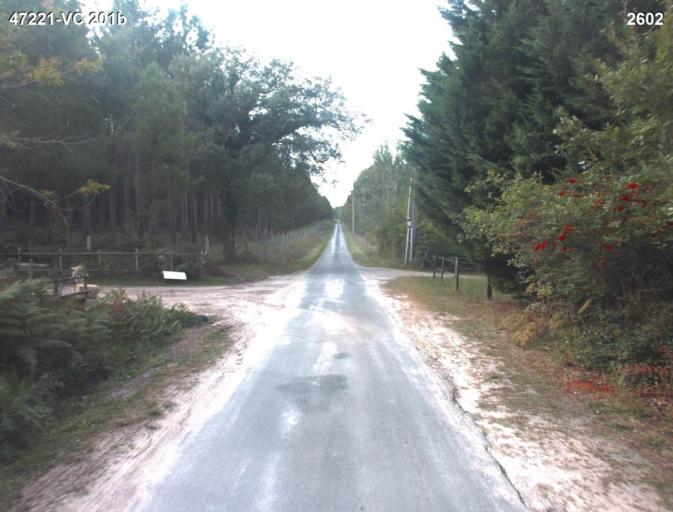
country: FR
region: Aquitaine
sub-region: Departement du Lot-et-Garonne
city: Mezin
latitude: 44.0849
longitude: 0.2215
